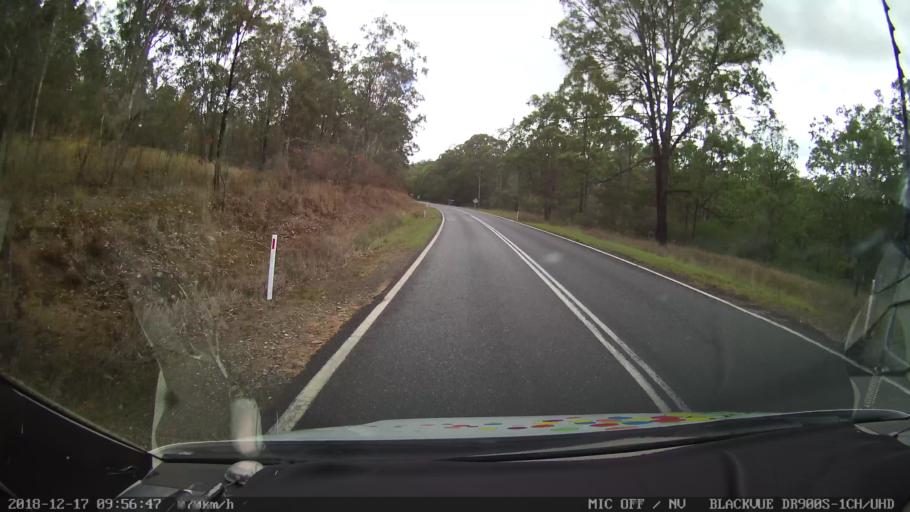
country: AU
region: New South Wales
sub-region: Tenterfield Municipality
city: Carrolls Creek
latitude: -28.9302
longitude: 152.3912
